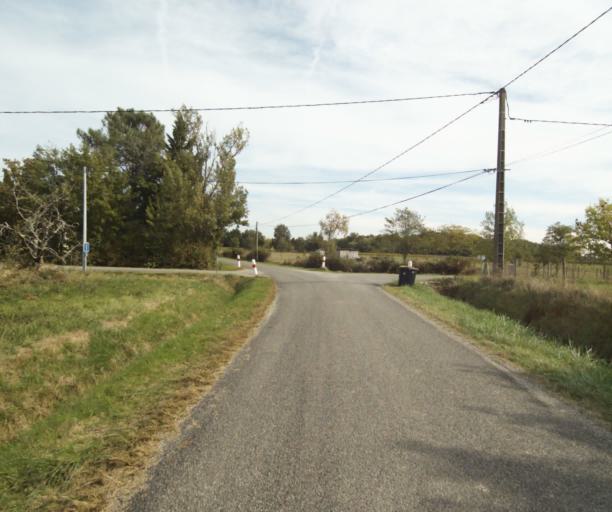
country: FR
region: Midi-Pyrenees
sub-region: Departement du Tarn-et-Garonne
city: Labastide-Saint-Pierre
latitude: 43.8803
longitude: 1.3685
